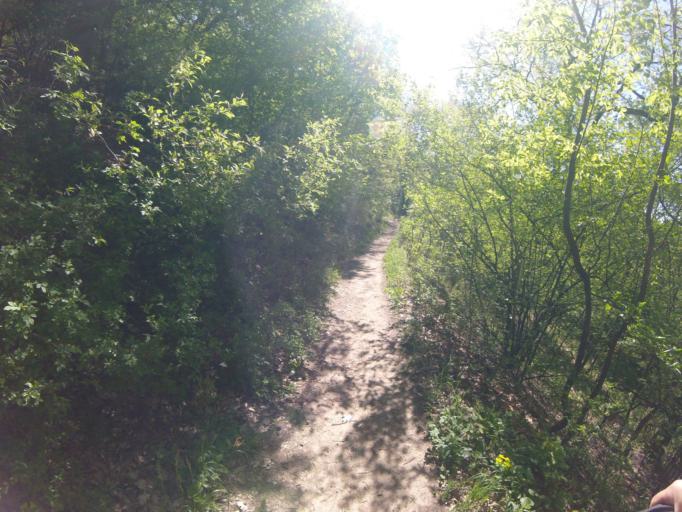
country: HU
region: Pest
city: Nagymaros
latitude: 47.7947
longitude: 18.9176
